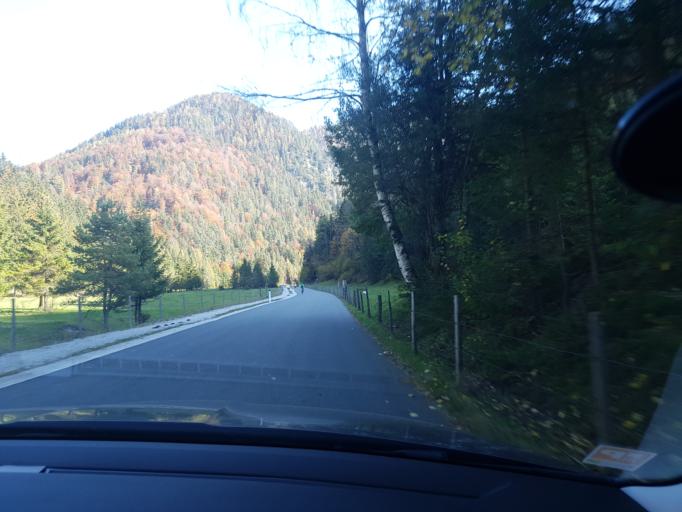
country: AT
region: Tyrol
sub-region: Politischer Bezirk Kitzbuhel
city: Hochfilzen
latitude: 47.5057
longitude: 12.6015
